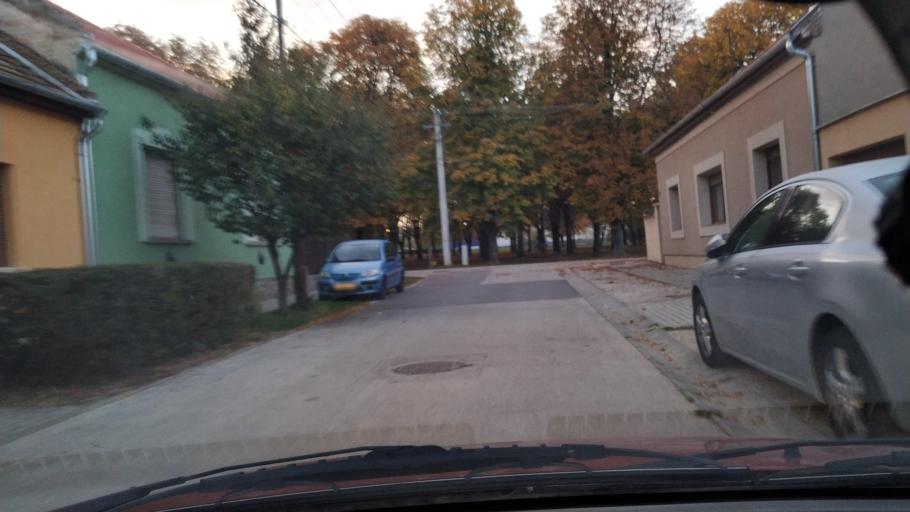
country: HU
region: Komarom-Esztergom
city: Esztergom
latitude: 47.7817
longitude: 18.7478
